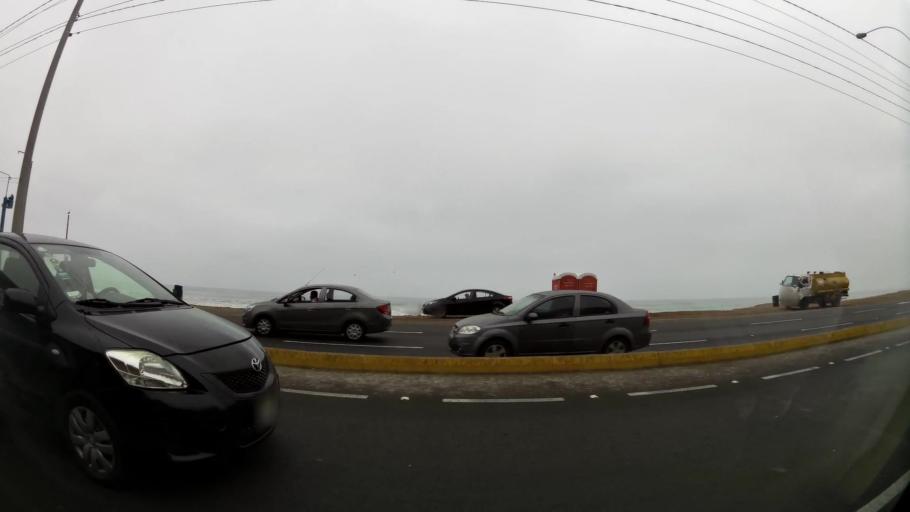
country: PE
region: Lima
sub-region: Lima
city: San Isidro
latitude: -12.1166
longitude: -77.0496
